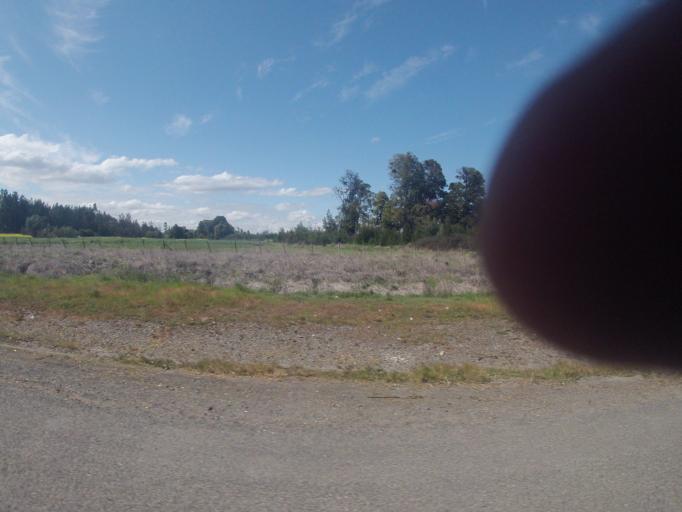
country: CL
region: Biobio
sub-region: Provincia de Biobio
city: Los Angeles
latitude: -37.4459
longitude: -72.4036
